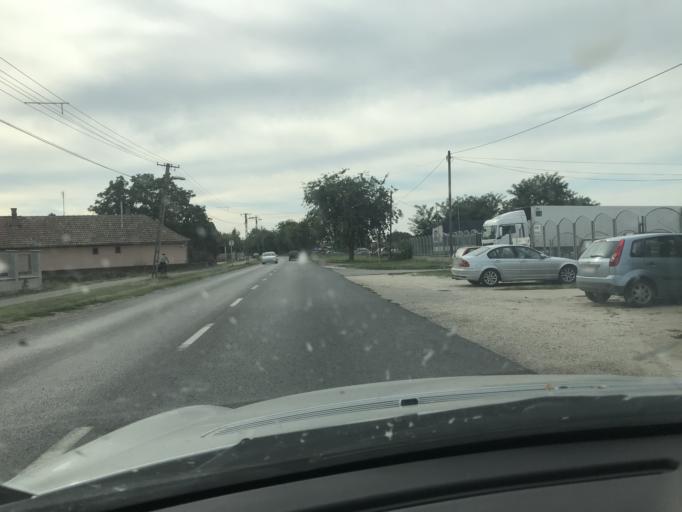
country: HU
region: Bacs-Kiskun
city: Kecel
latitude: 46.5202
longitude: 19.2308
